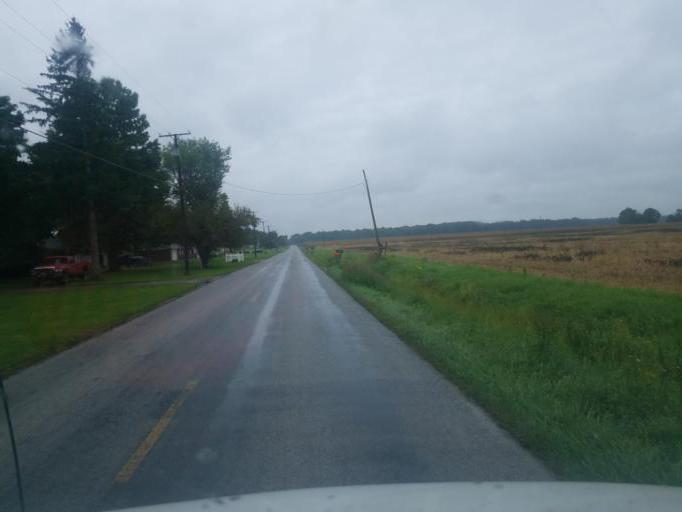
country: US
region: Ohio
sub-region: Medina County
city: Seville
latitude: 40.9824
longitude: -81.8609
